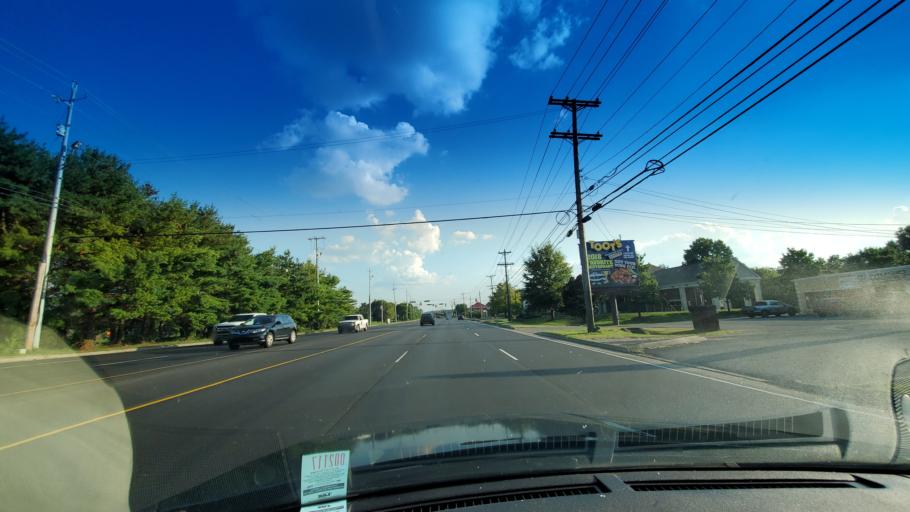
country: US
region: Tennessee
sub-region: Rutherford County
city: Murfreesboro
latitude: 35.7965
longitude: -86.3990
